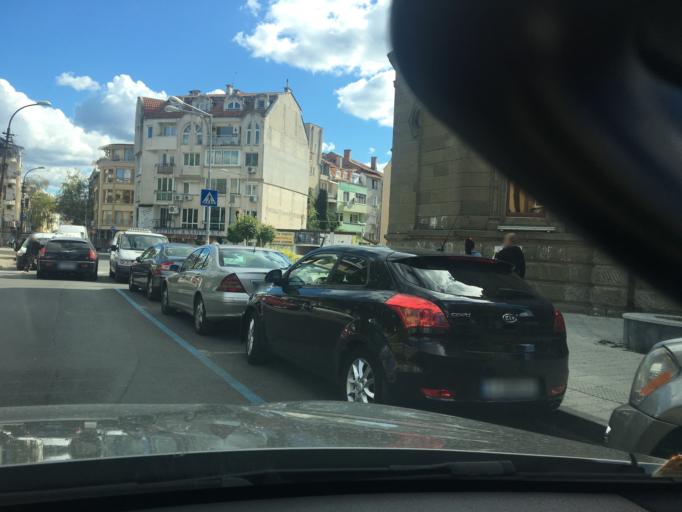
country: BG
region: Burgas
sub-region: Obshtina Burgas
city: Burgas
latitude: 42.4965
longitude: 27.4742
